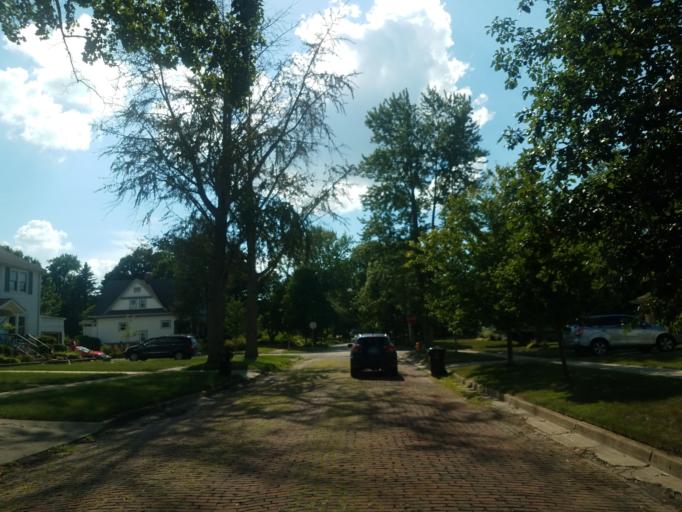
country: US
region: Illinois
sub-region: McLean County
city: Bloomington
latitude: 40.4764
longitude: -88.9646
